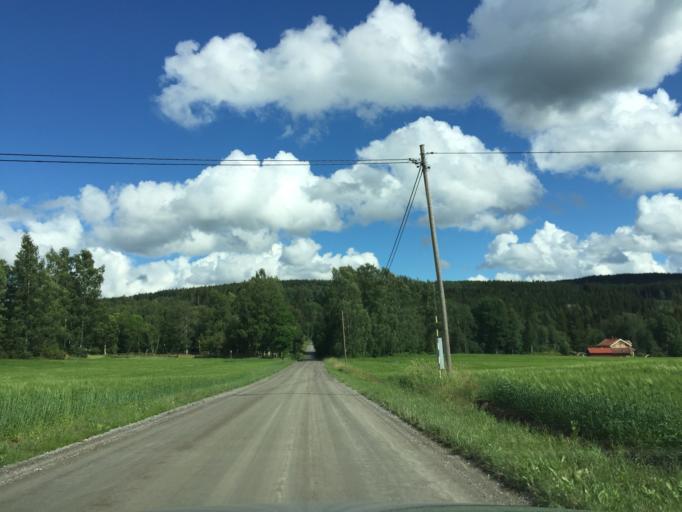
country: NO
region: Hedmark
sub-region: Kongsvinger
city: Spetalen
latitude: 60.2502
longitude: 11.8601
